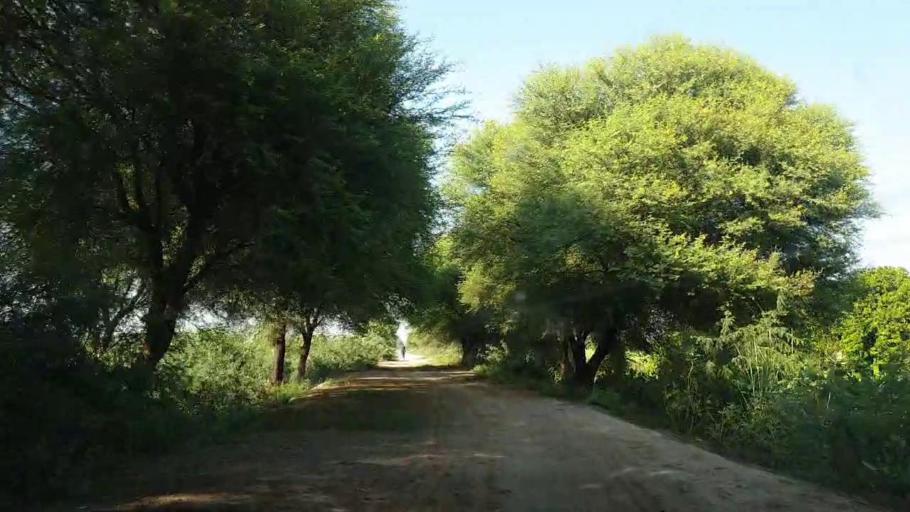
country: PK
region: Sindh
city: Tando Jam
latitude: 25.3628
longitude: 68.5695
